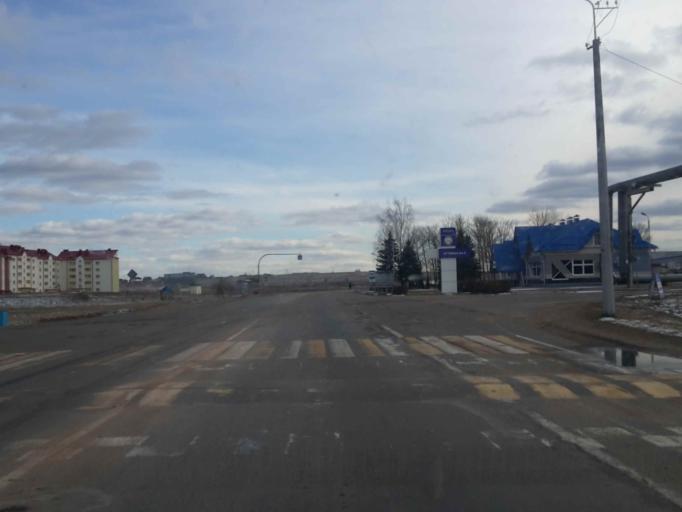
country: BY
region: Minsk
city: Myadzyel
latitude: 54.8772
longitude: 26.9409
